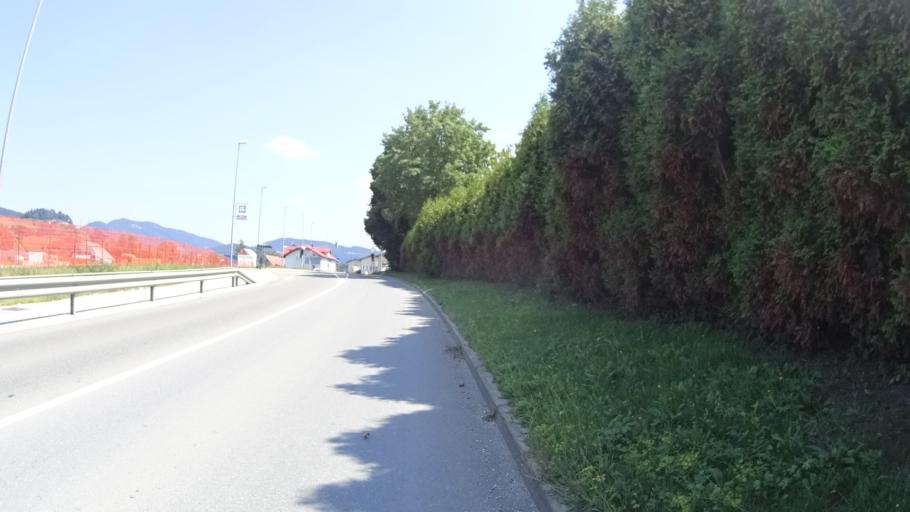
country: SI
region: Prevalje
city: Prevalje
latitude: 46.5445
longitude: 14.9425
